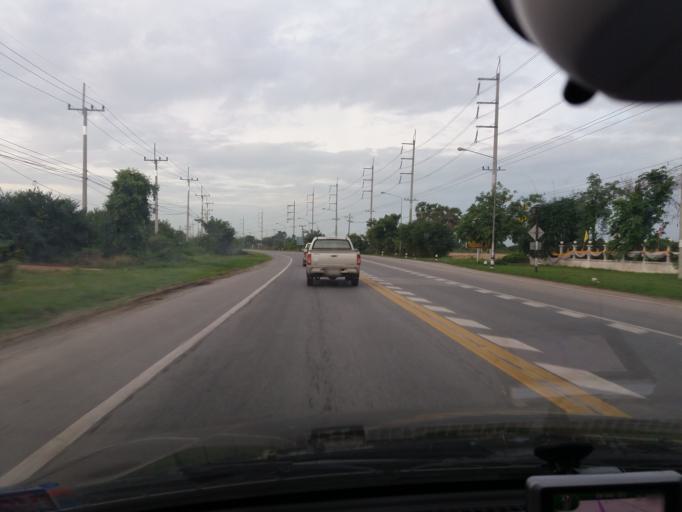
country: TH
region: Suphan Buri
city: U Thong
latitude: 14.5099
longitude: 99.9163
